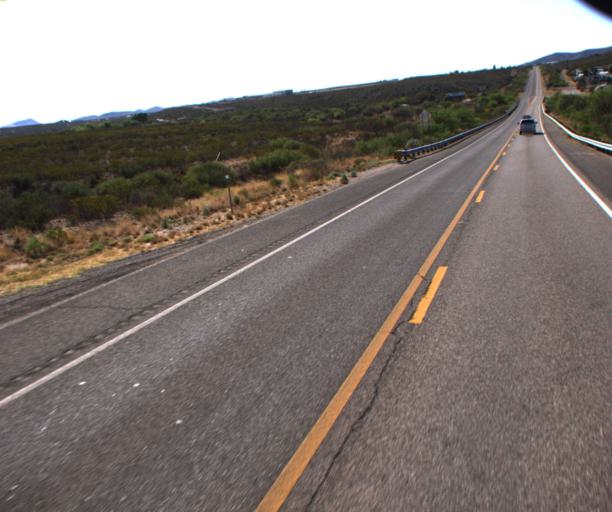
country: US
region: Arizona
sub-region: Cochise County
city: Tombstone
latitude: 31.7335
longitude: -110.0817
